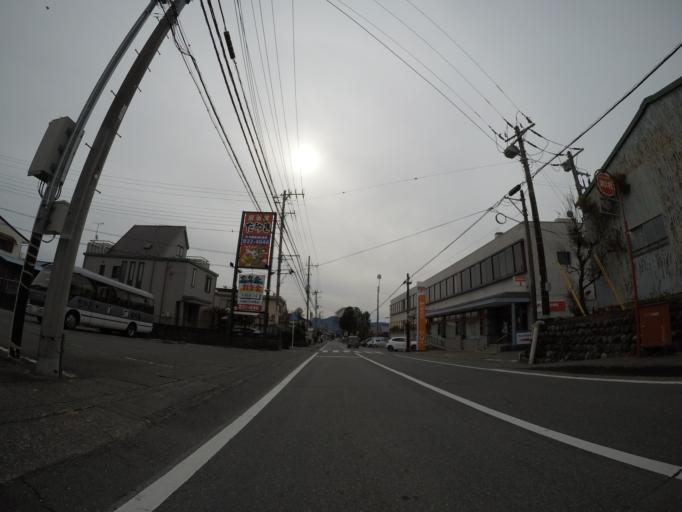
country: JP
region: Shizuoka
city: Fujinomiya
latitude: 35.2292
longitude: 138.6204
